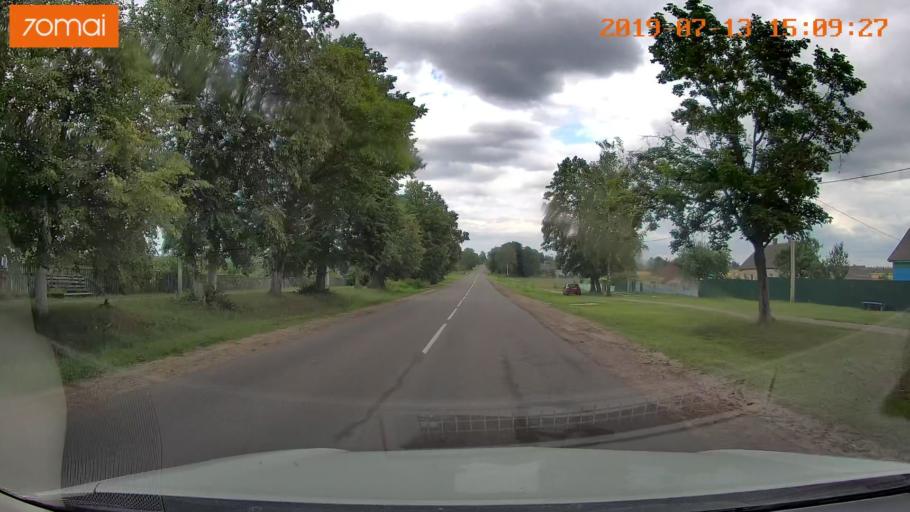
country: BY
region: Mogilev
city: Hlusha
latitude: 53.1729
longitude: 28.7623
